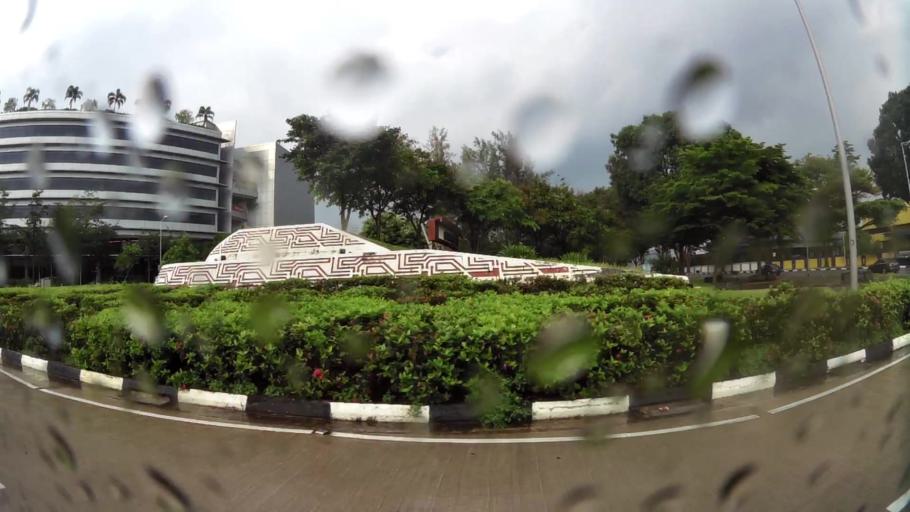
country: SG
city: Singapore
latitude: 1.3365
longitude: 103.9687
